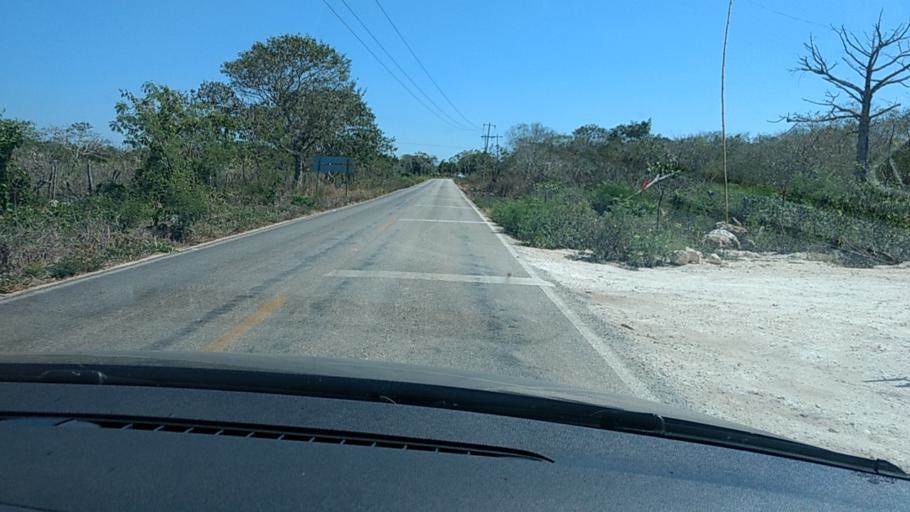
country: MX
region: Yucatan
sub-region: Tizimin
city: Tizimin
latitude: 21.1943
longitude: -88.1706
